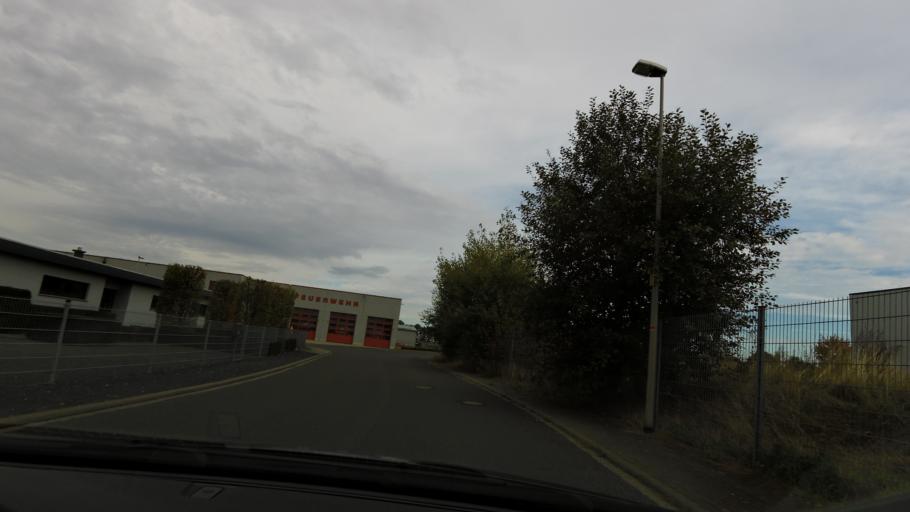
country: DE
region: North Rhine-Westphalia
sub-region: Regierungsbezirk Koln
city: Gangelt
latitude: 50.9915
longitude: 5.9839
